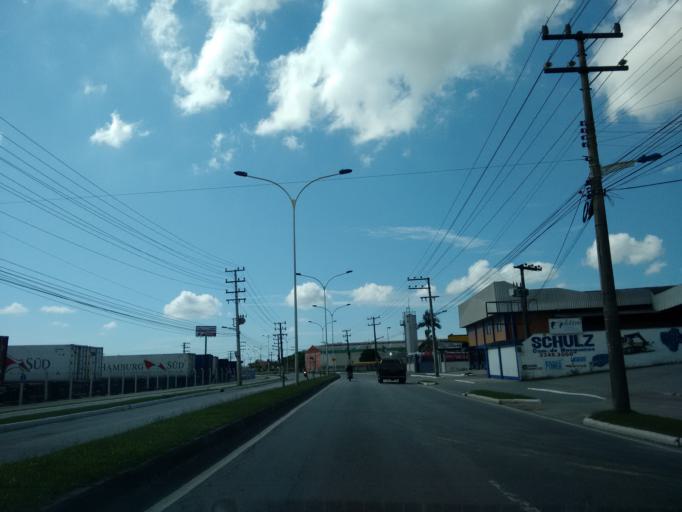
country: BR
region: Santa Catarina
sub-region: Itajai
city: Itajai
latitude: -26.8910
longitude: -48.7126
